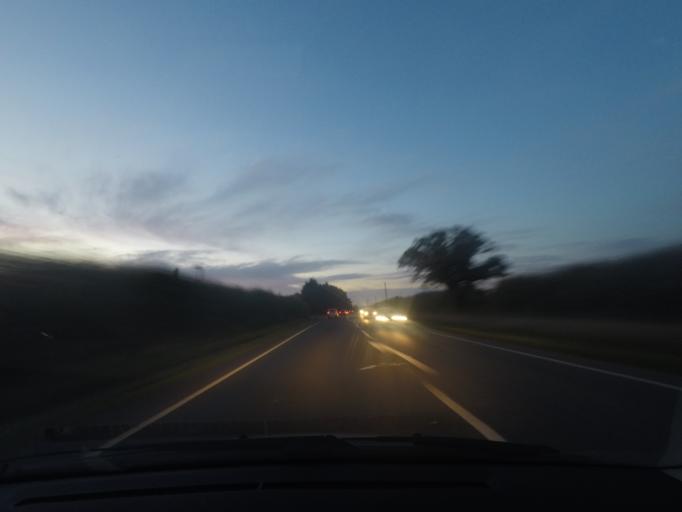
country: GB
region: England
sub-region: East Riding of Yorkshire
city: Wilberfoss
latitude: 53.9400
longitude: -0.8631
